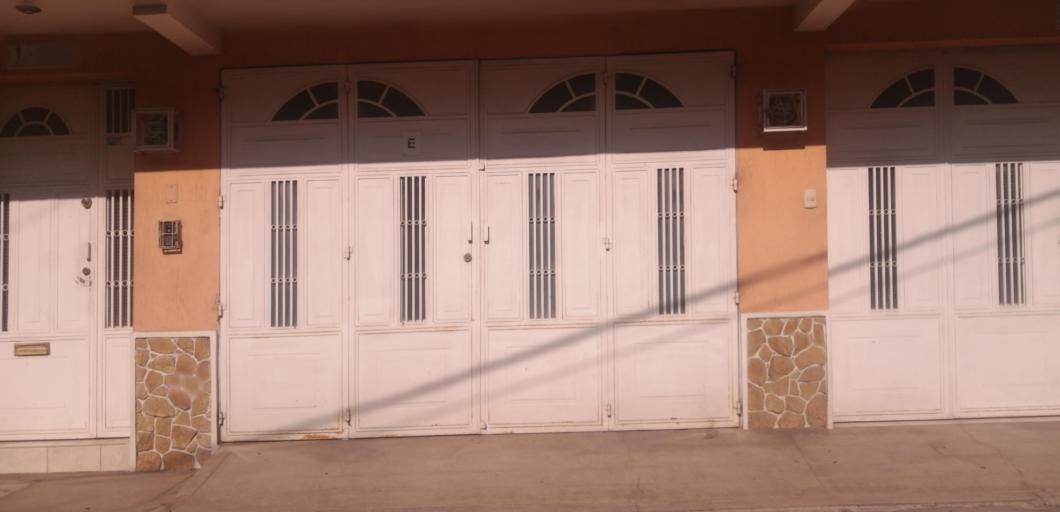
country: GT
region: Quetzaltenango
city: Quetzaltenango
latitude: 14.8407
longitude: -91.5322
